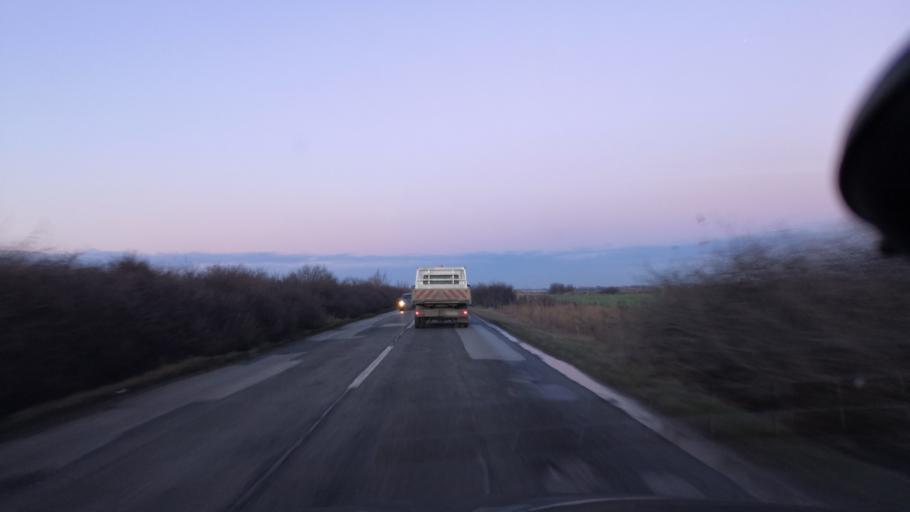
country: RS
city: Vojka
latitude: 44.9127
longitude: 20.1398
